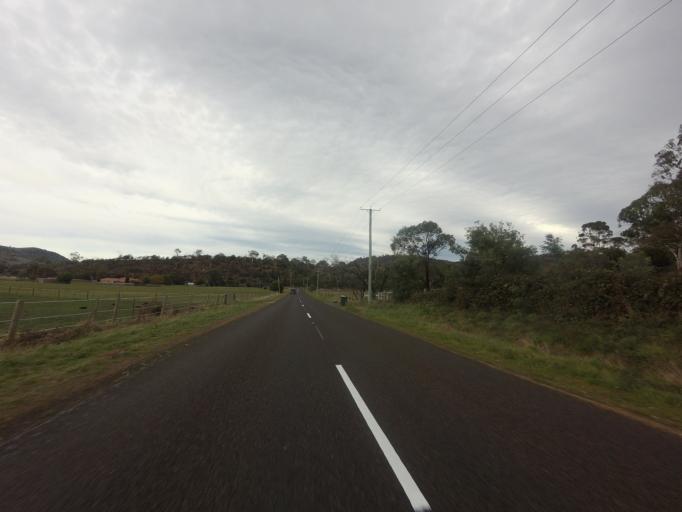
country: AU
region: Tasmania
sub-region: Brighton
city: Bridgewater
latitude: -42.6748
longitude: 147.1545
